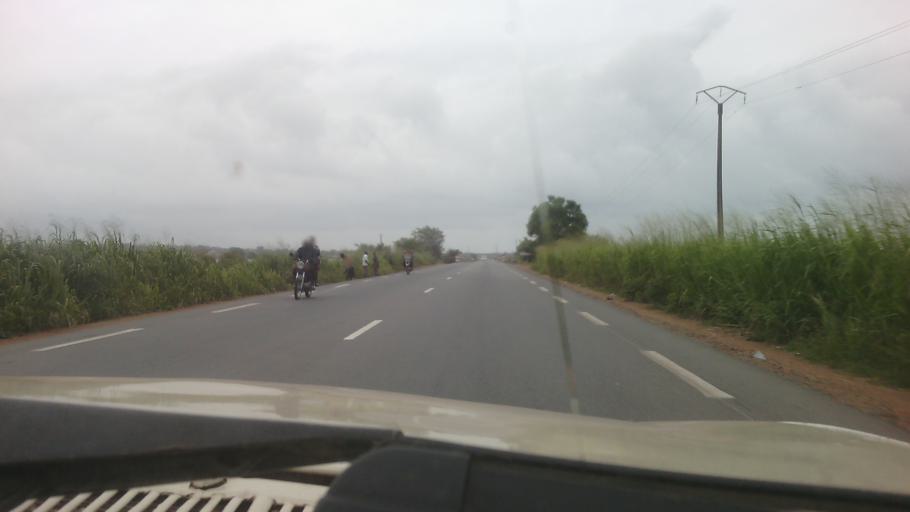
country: BJ
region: Mono
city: Come
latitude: 6.3973
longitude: 1.9260
